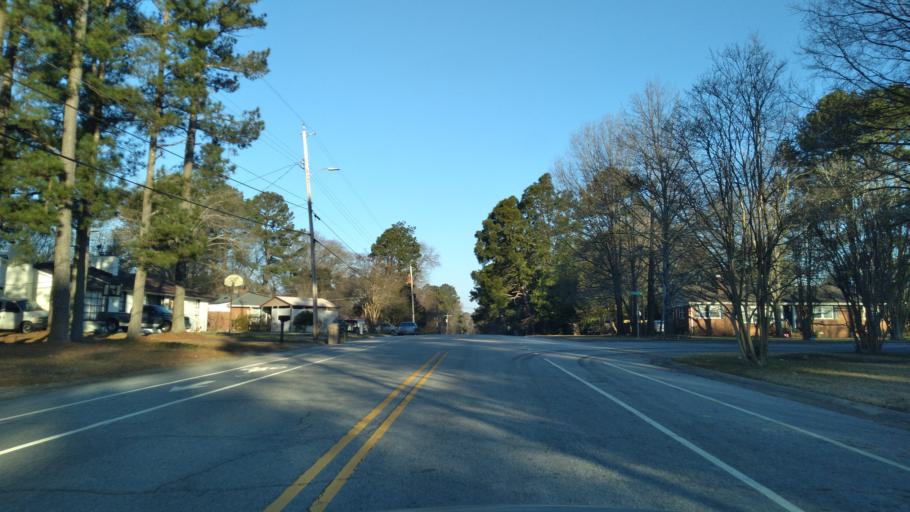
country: US
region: North Carolina
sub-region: Wake County
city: Garner
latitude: 35.6983
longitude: -78.6210
